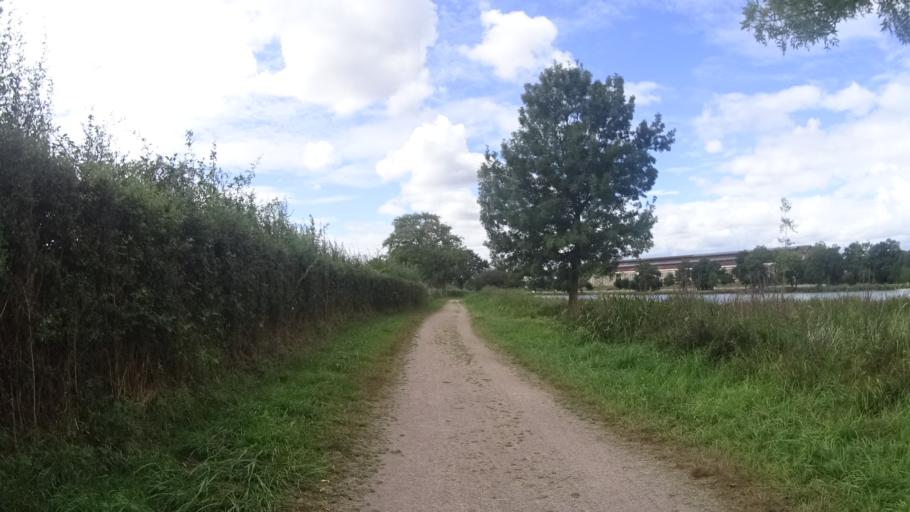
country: FR
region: Bourgogne
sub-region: Departement de Saone-et-Loire
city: Saint-Leu
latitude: 46.7426
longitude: 4.4912
